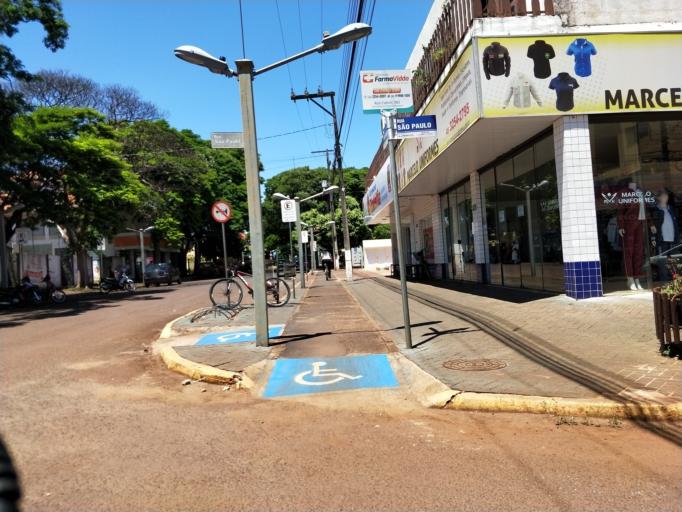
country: BR
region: Parana
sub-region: Marechal Candido Rondon
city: Marechal Candido Rondon
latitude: -24.5603
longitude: -54.0605
